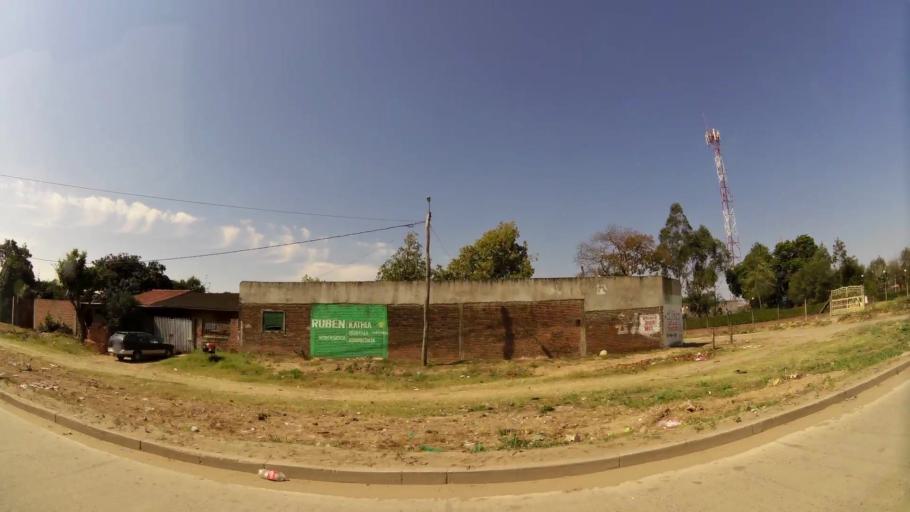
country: BO
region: Santa Cruz
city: Santa Cruz de la Sierra
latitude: -17.7549
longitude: -63.1204
